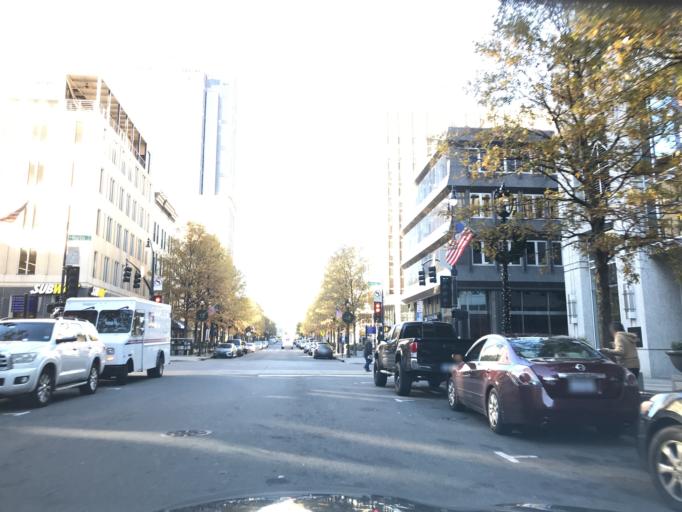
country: US
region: North Carolina
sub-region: Wake County
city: Raleigh
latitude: 35.7765
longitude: -78.6393
